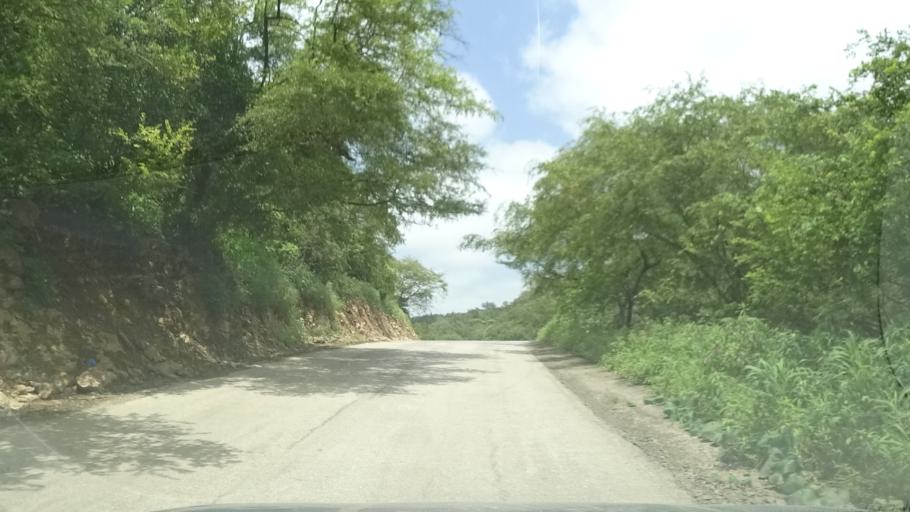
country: OM
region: Zufar
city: Salalah
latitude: 17.1761
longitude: 54.1649
